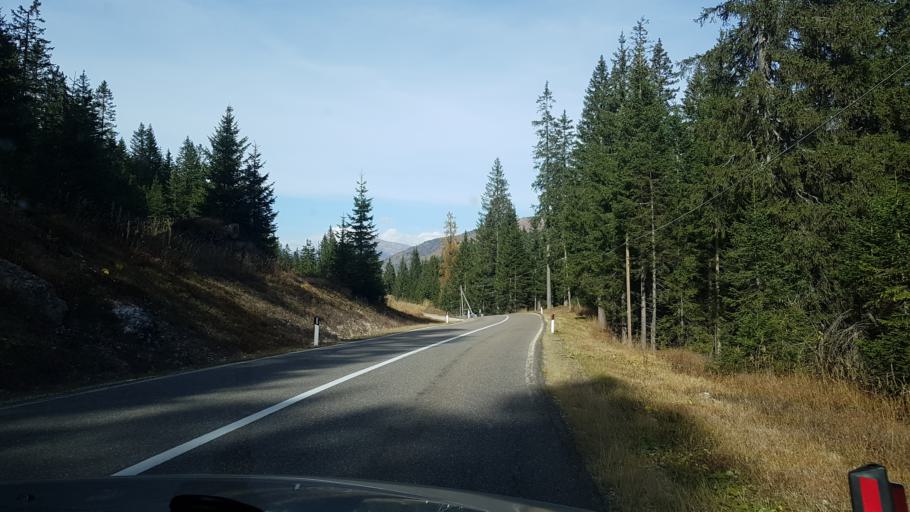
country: IT
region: Trentino-Alto Adige
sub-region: Bolzano
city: Sesto
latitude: 46.6612
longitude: 12.4037
